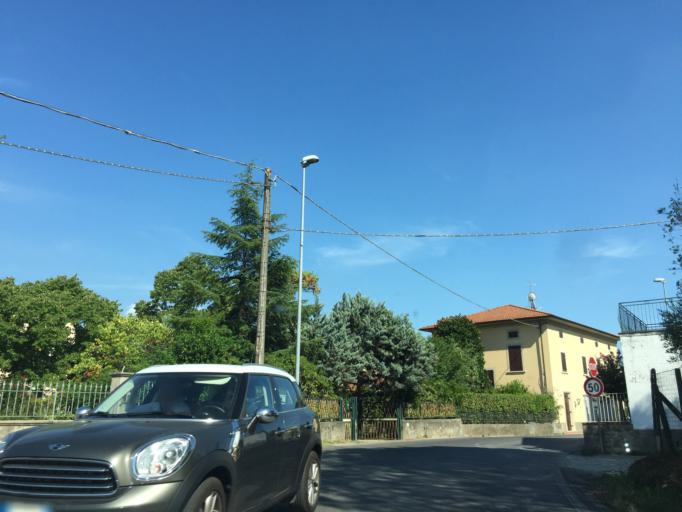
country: IT
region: Tuscany
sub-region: Provincia di Pistoia
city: San Rocco
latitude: 43.8297
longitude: 10.8611
